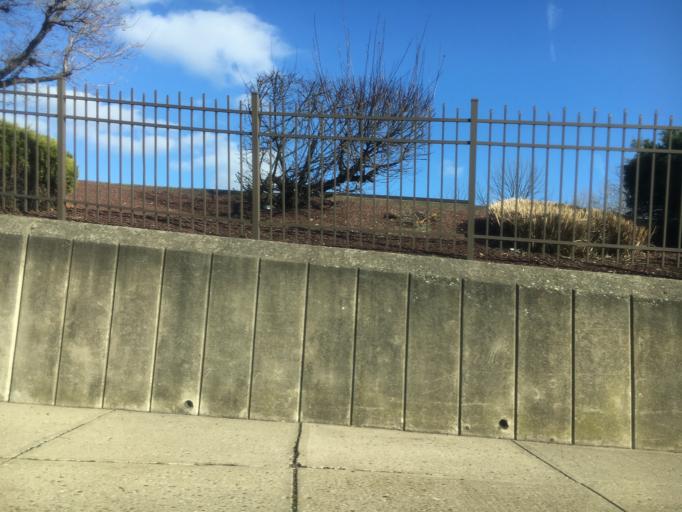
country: US
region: Pennsylvania
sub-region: Northampton County
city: Northampton
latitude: 40.6790
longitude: -75.4888
